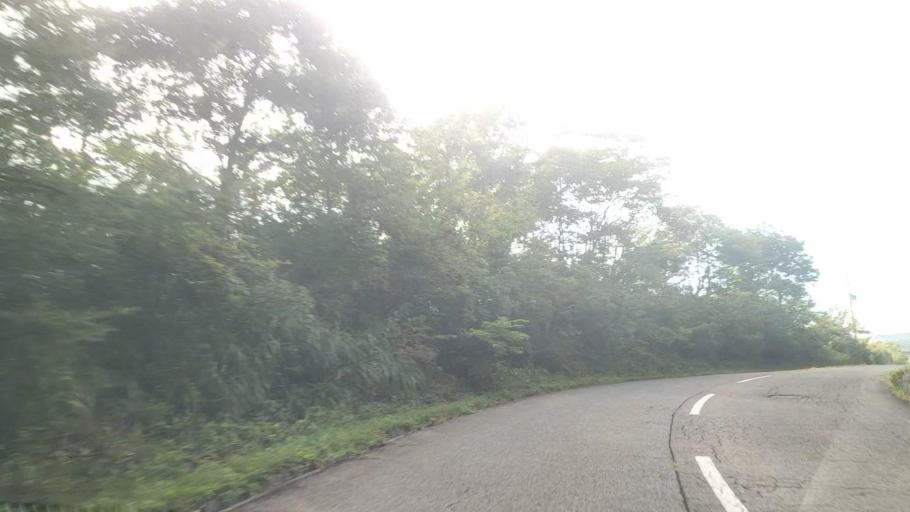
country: JP
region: Nagano
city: Iiyama
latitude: 36.8198
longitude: 138.4208
